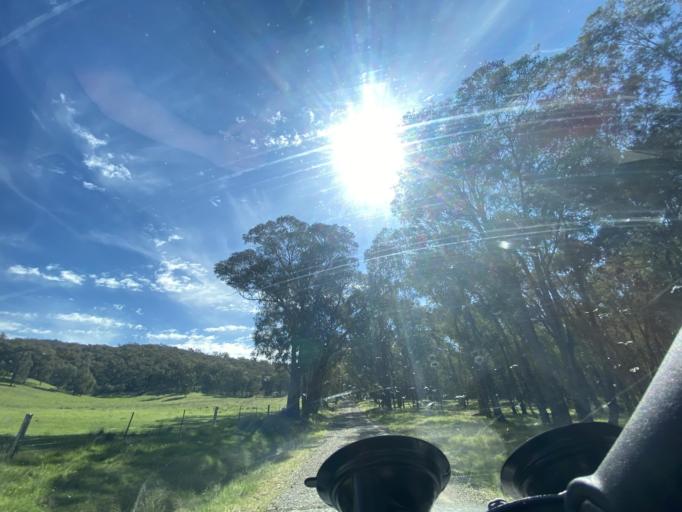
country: AU
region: Victoria
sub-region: Mansfield
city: Mansfield
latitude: -36.8061
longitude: 146.1240
